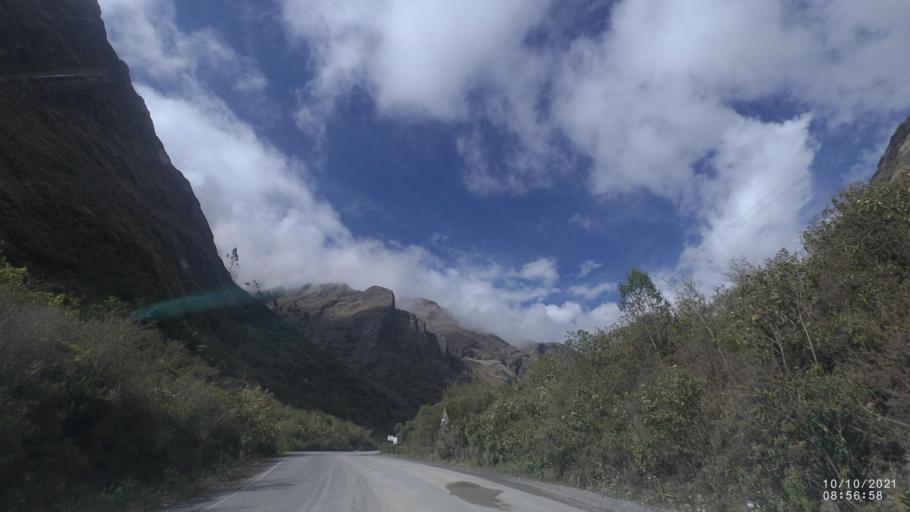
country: BO
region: La Paz
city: Quime
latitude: -16.9915
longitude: -67.2482
